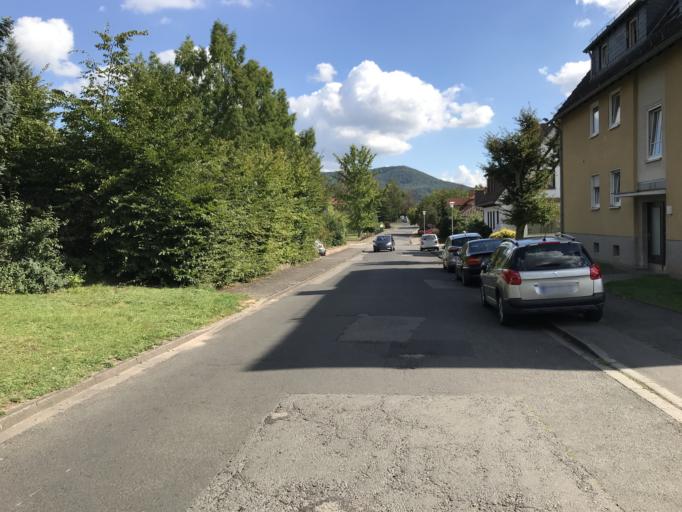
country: DE
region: Hesse
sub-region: Regierungsbezirk Kassel
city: Bad Sooden-Allendorf
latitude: 51.2683
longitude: 9.9845
